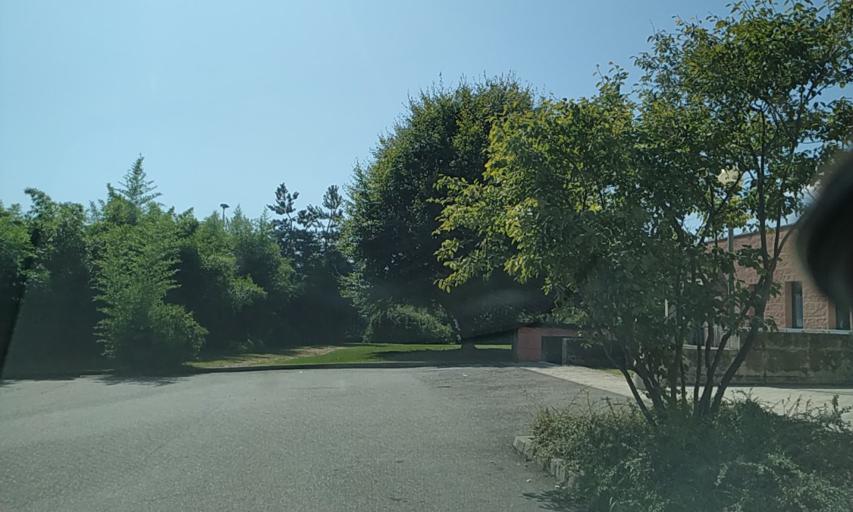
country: IT
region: Piedmont
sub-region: Provincia di Biella
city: Ceresane-Curanuova
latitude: 45.5260
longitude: 8.0071
